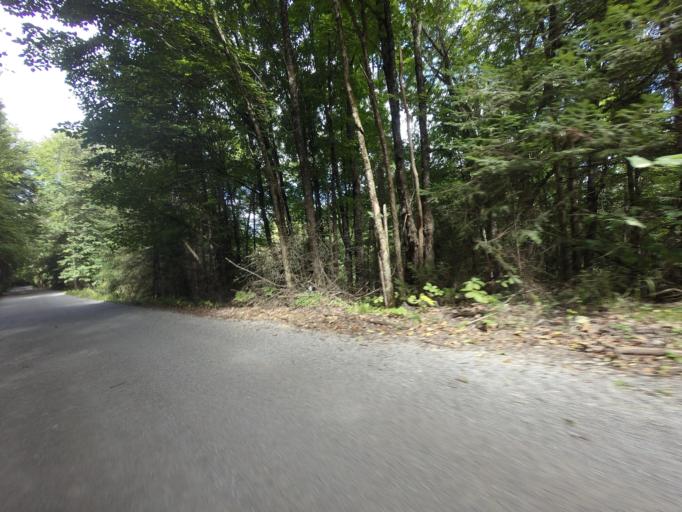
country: CA
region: Ontario
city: Omemee
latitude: 44.7520
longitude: -78.6703
